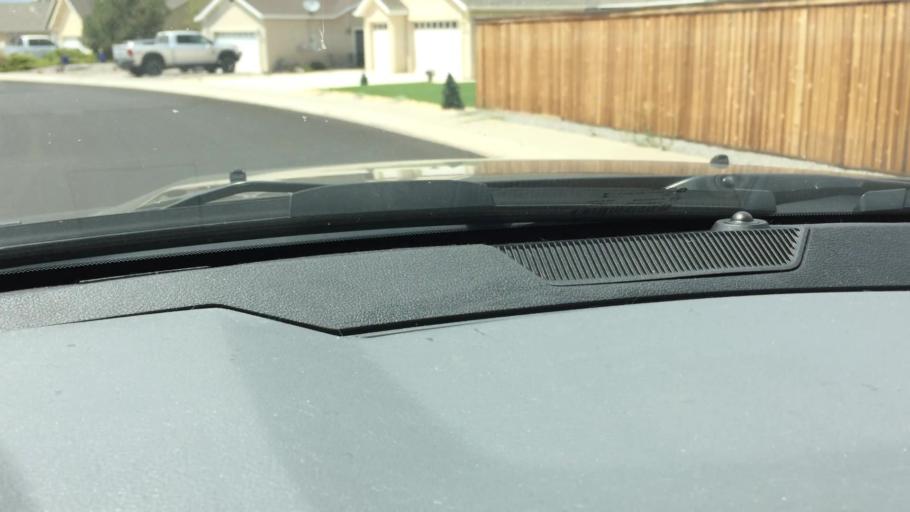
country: US
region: Nevada
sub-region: Lyon County
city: Fernley
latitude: 39.5885
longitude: -119.1522
